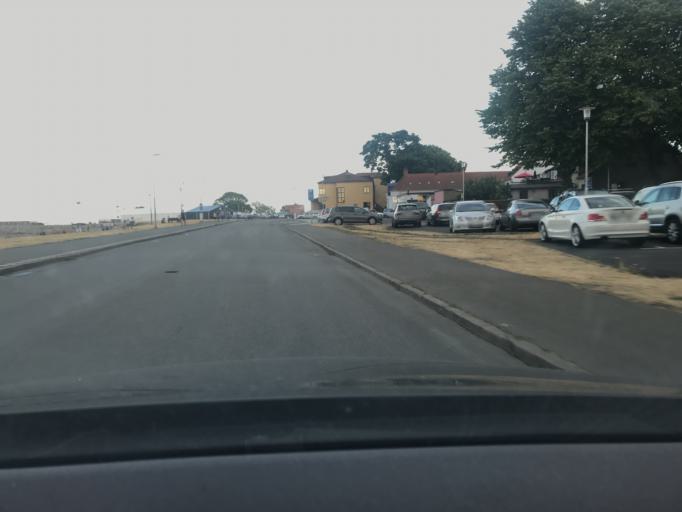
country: SE
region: Skane
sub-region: Simrishamns Kommun
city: Simrishamn
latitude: 55.5597
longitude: 14.3505
